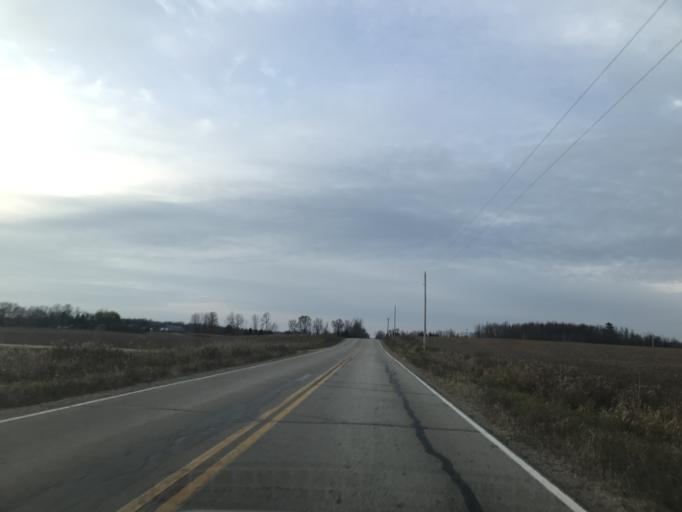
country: US
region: Wisconsin
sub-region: Marinette County
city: Peshtigo
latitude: 45.0960
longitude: -87.7994
